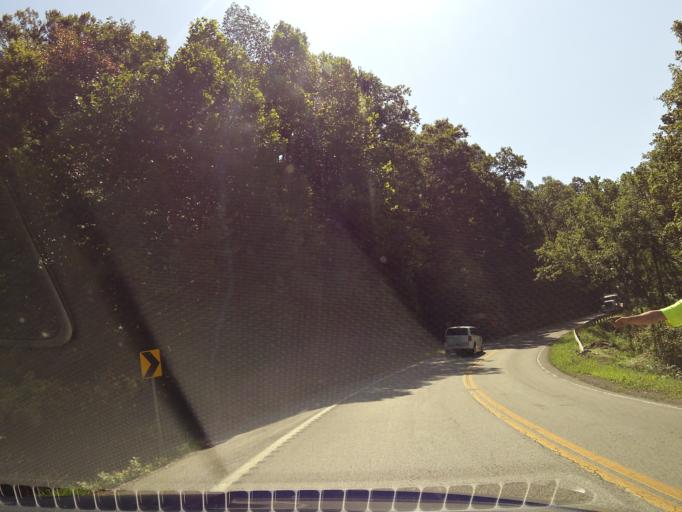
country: US
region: Kentucky
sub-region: Clay County
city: Manchester
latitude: 37.0890
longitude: -83.6913
